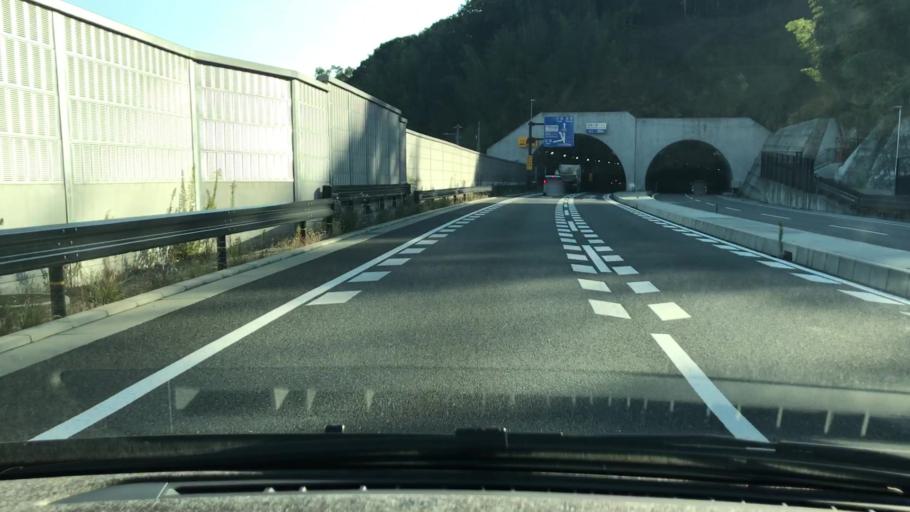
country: JP
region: Hyogo
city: Takarazuka
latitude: 34.8283
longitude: 135.3007
